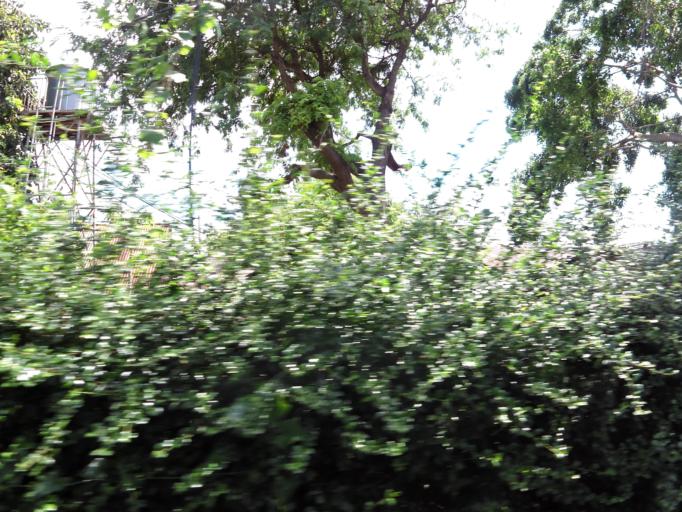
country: TH
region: Phuket
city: Ban Chalong
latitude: 7.8260
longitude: 98.3389
